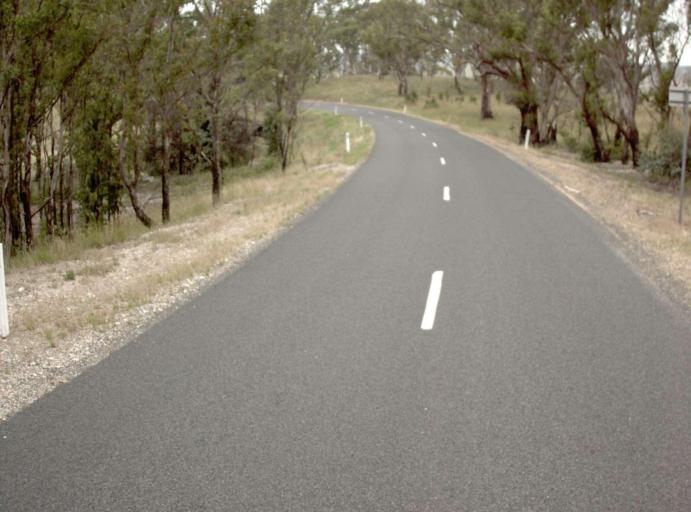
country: AU
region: Victoria
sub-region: Wellington
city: Heyfield
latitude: -37.8737
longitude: 146.7095
